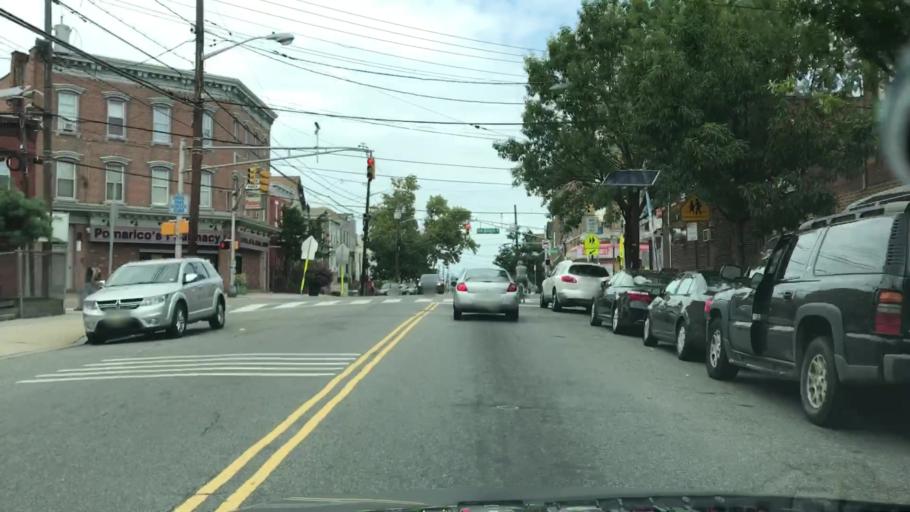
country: US
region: New Jersey
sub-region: Hudson County
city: Jersey City
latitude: 40.6975
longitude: -74.0922
